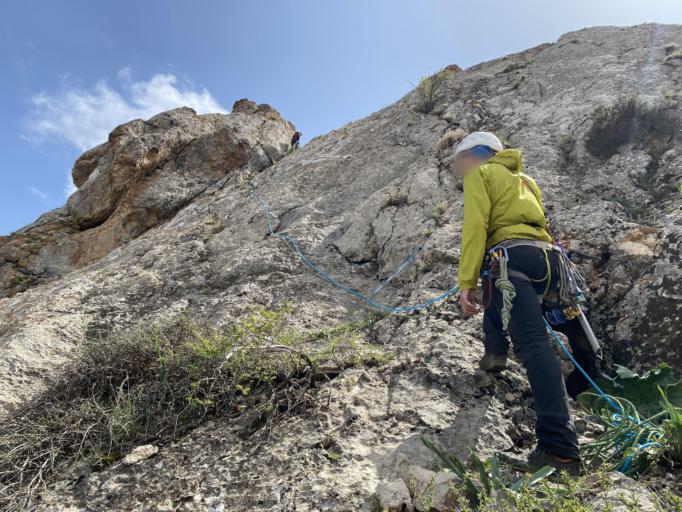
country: KZ
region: Ongtustik Qazaqstan
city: Ashchysay
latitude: 43.7436
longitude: 68.8396
